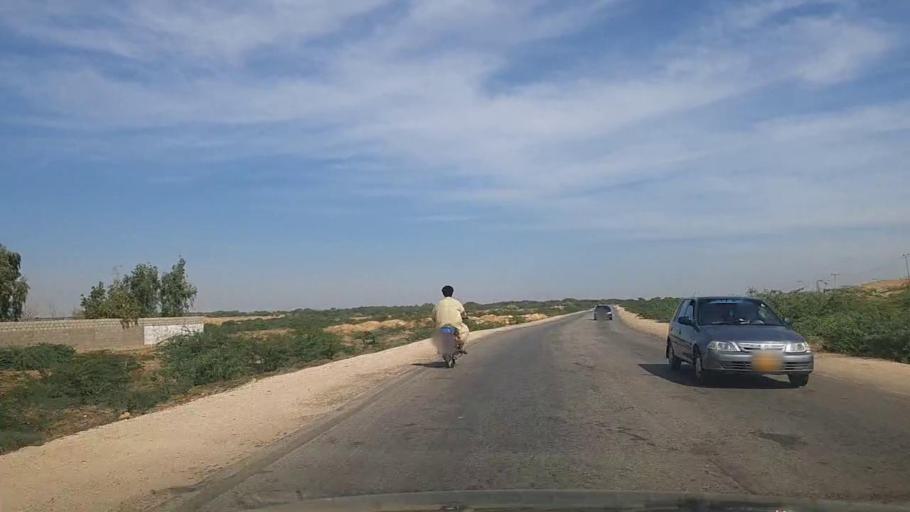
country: PK
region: Sindh
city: Daro Mehar
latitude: 24.9912
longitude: 68.1428
